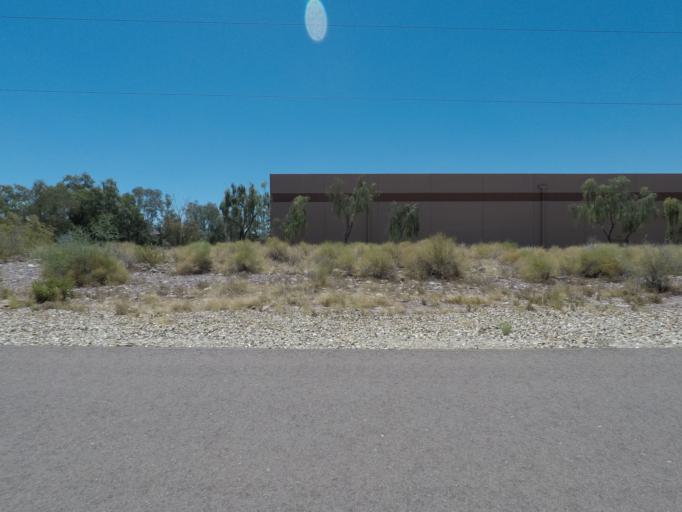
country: US
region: Arizona
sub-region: Maricopa County
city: Tempe Junction
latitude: 33.4253
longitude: -112.0015
